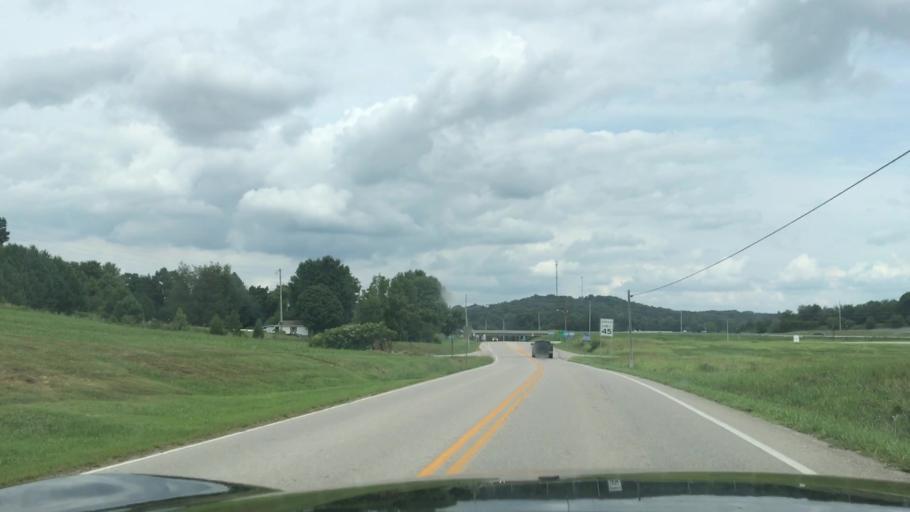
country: US
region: Kentucky
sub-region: Butler County
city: Morgantown
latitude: 37.2122
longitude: -86.7147
